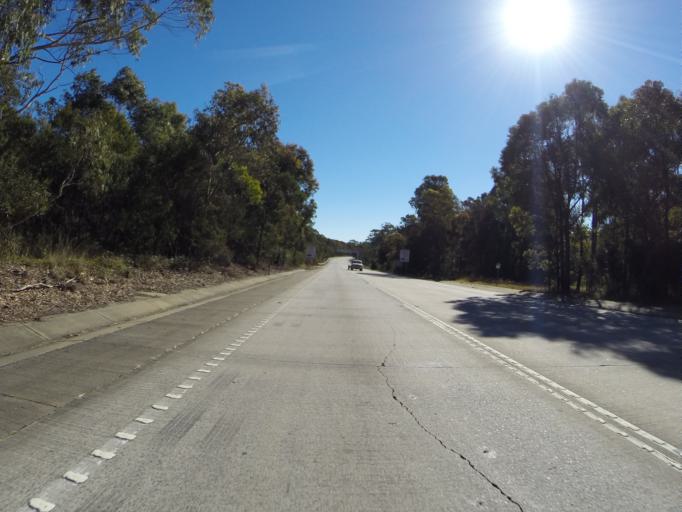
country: AU
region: New South Wales
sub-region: Wollondilly
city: Douglas Park
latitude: -34.2747
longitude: 150.7149
